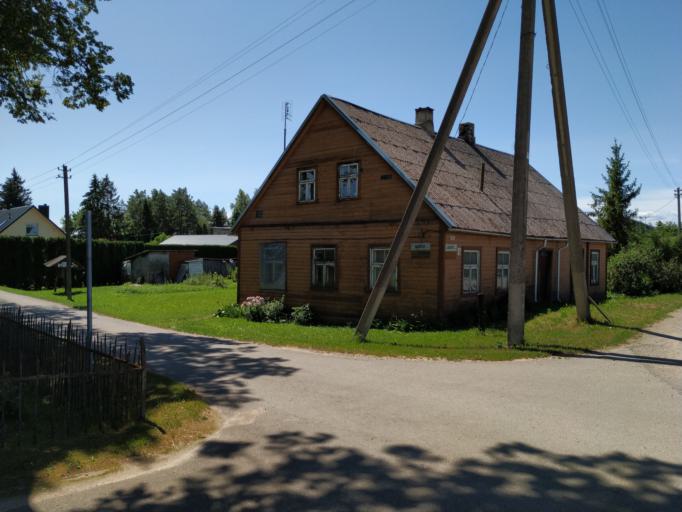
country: LT
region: Panevezys
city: Pasvalys
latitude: 56.2272
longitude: 24.4038
